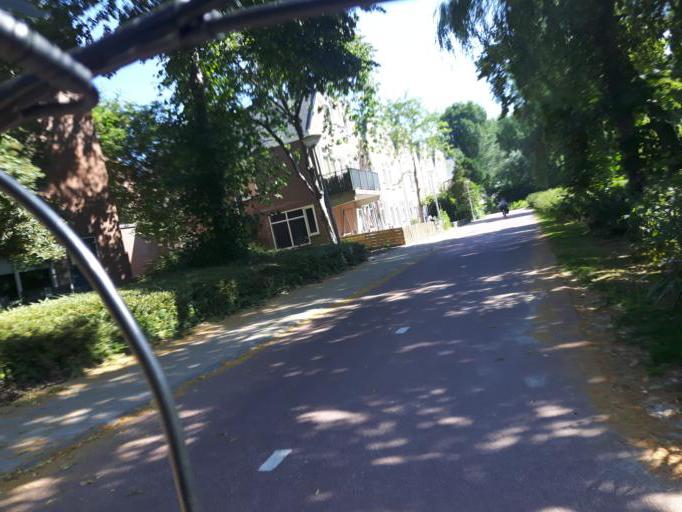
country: NL
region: Zeeland
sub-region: Gemeente Middelburg
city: Middelburg
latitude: 51.4941
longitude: 3.6228
